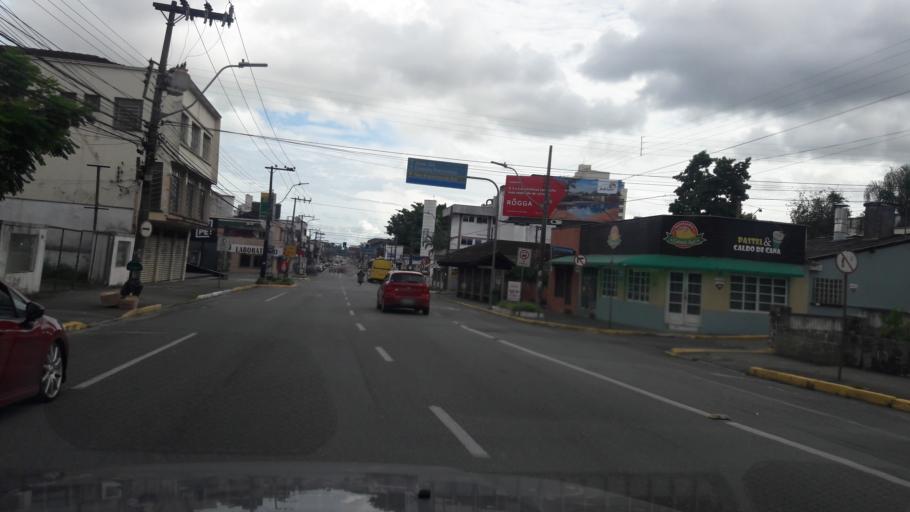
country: BR
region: Santa Catarina
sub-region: Joinville
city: Joinville
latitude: -26.3081
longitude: -48.8456
